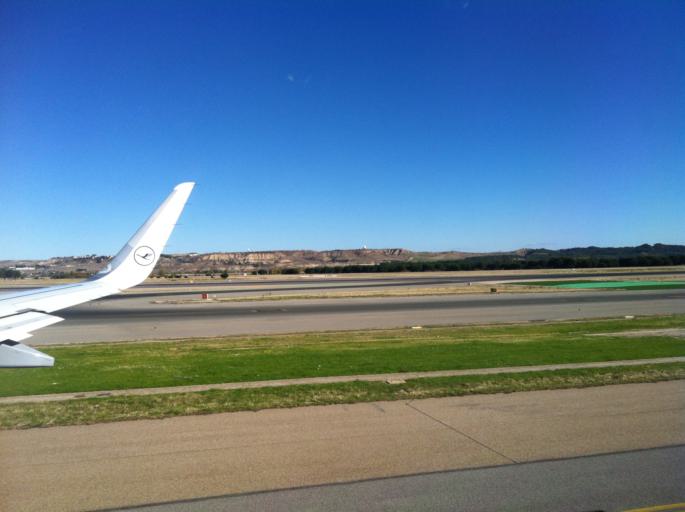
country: ES
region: Madrid
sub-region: Provincia de Madrid
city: Barajas de Madrid
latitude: 40.4770
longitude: -3.5720
